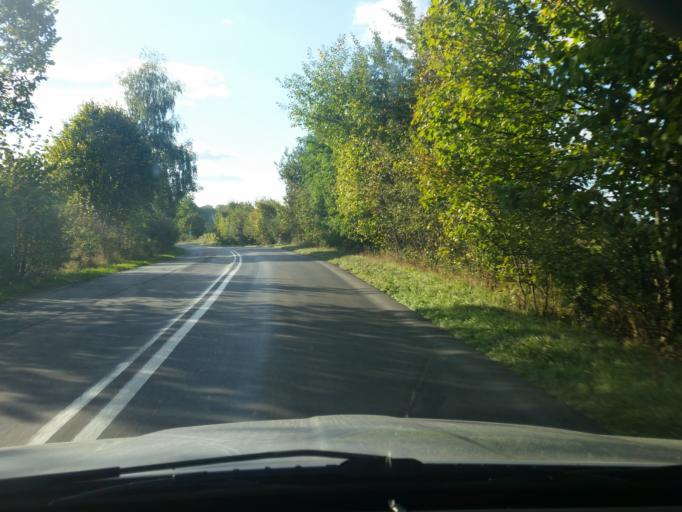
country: PL
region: Pomeranian Voivodeship
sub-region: Powiat chojnicki
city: Chojnice
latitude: 53.7200
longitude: 17.5027
